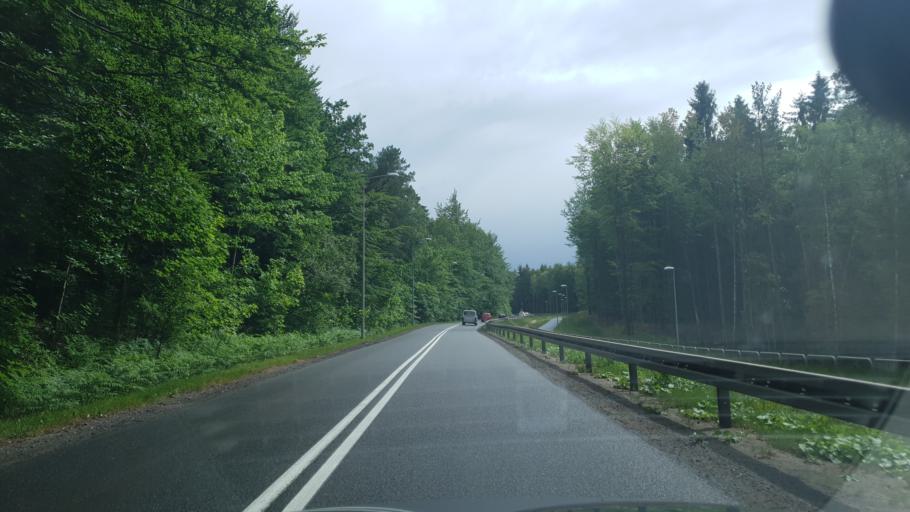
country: PL
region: Pomeranian Voivodeship
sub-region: Powiat kartuski
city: Kartuzy
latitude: 54.3493
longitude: 18.2163
